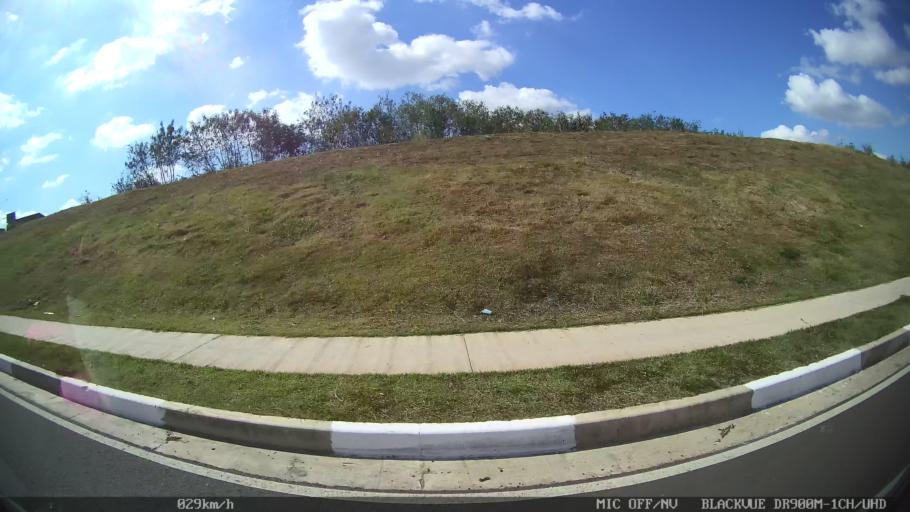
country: BR
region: Sao Paulo
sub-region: Hortolandia
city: Hortolandia
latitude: -22.8842
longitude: -47.2122
